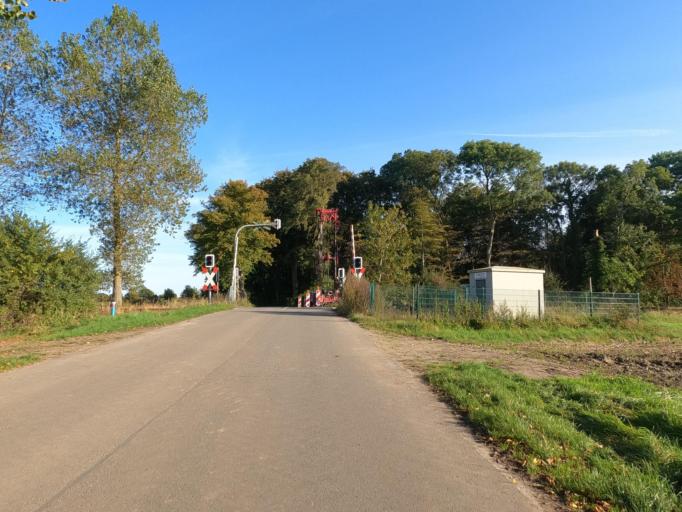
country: DE
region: Schleswig-Holstein
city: Neukirchen
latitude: 54.3177
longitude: 11.0198
